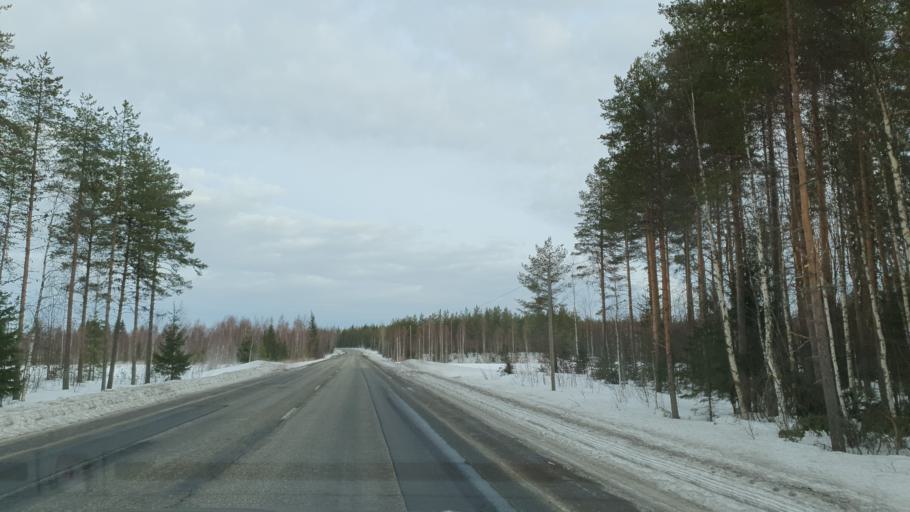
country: FI
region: Kainuu
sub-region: Kajaani
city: Vuokatti
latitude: 64.1950
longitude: 28.1727
